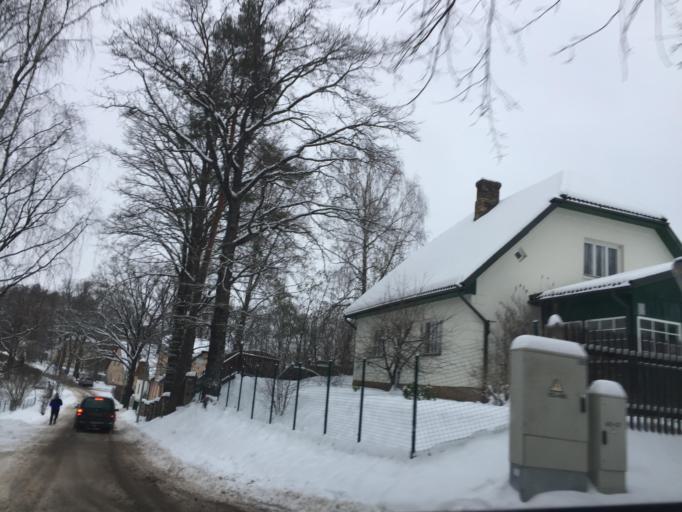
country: LV
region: Smiltene
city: Smiltene
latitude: 57.4213
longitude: 25.8985
